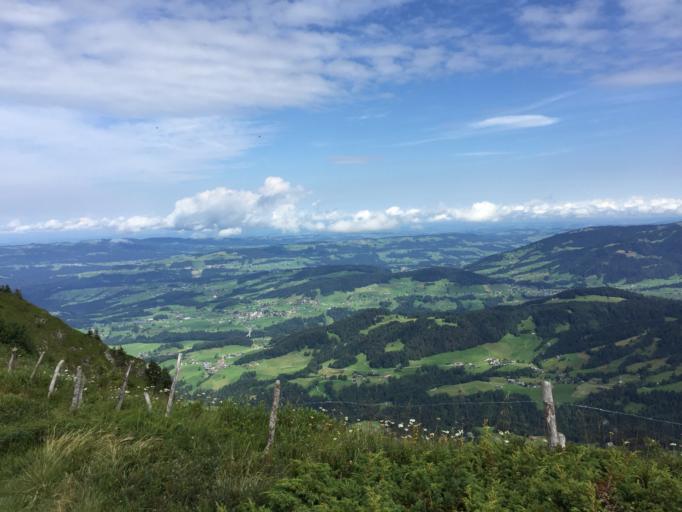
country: AT
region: Vorarlberg
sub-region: Politischer Bezirk Bregenz
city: Bizau
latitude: 47.4018
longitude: 9.9471
